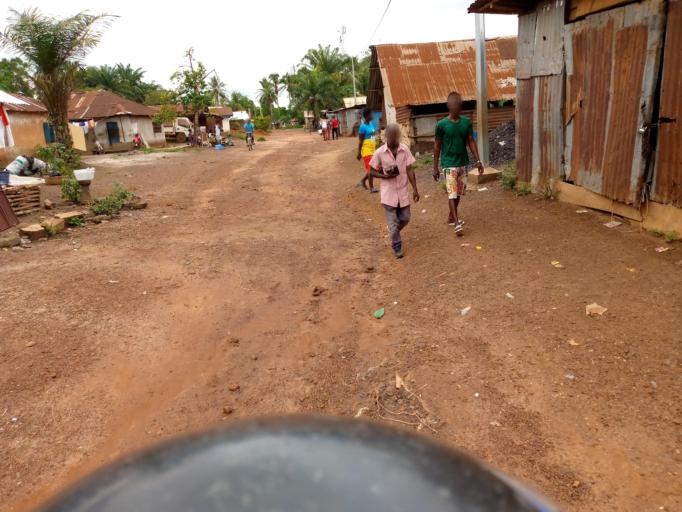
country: SL
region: Southern Province
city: Mogbwemo
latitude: 7.7866
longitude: -12.2965
